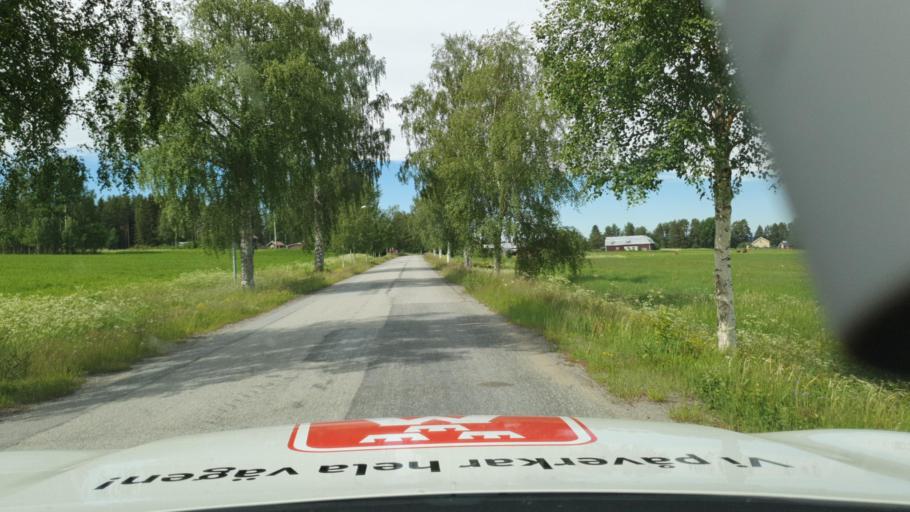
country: SE
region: Vaesterbotten
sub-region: Skelleftea Kommun
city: Burtraesk
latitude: 64.4254
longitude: 20.5328
